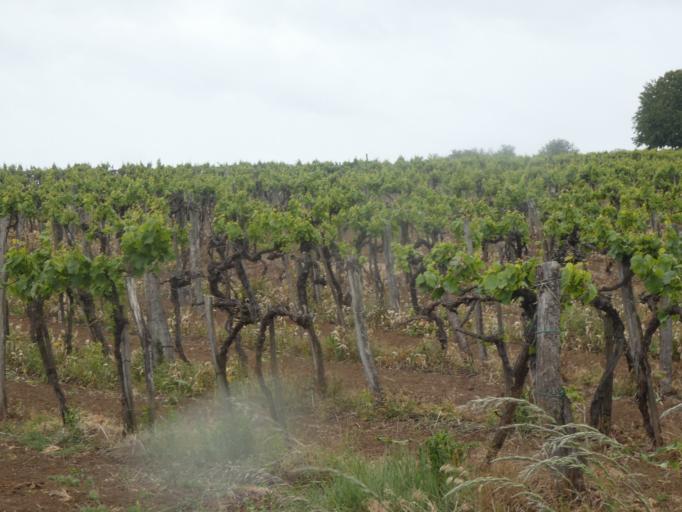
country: HU
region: Pest
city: Kerepes
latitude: 47.5914
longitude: 19.2744
